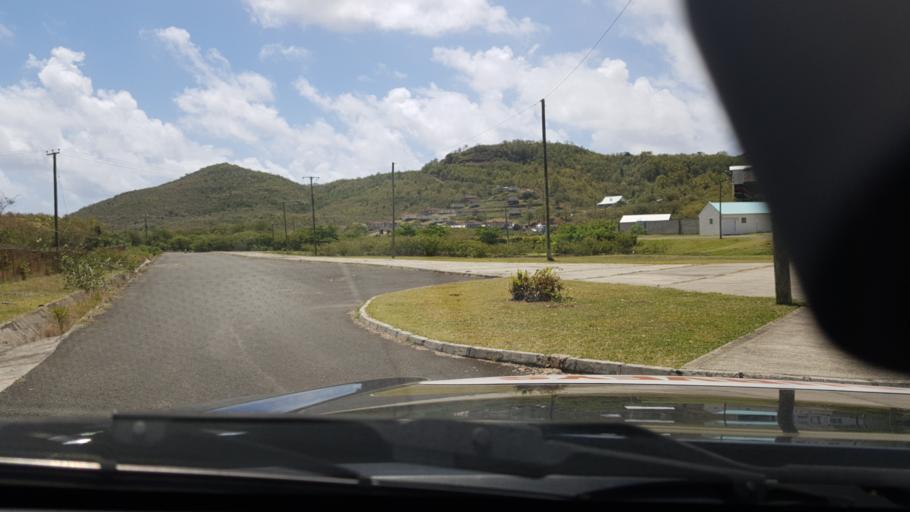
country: LC
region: Gros-Islet
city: Gros Islet
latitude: 14.0725
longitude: -60.9330
